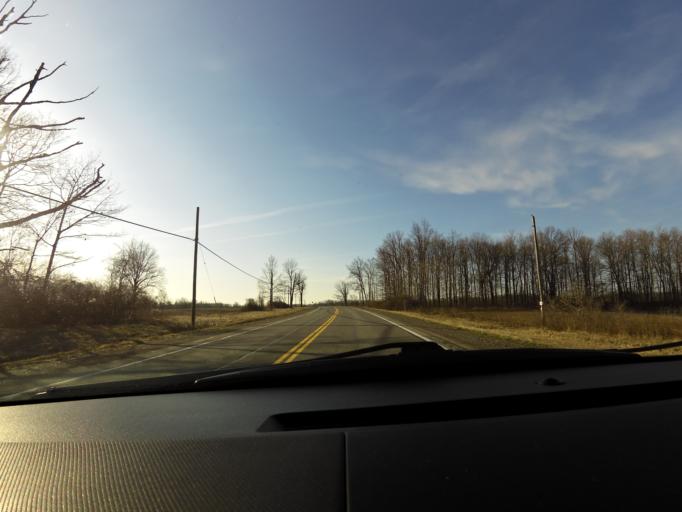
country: CA
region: Ontario
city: Ancaster
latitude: 42.9743
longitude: -79.8711
